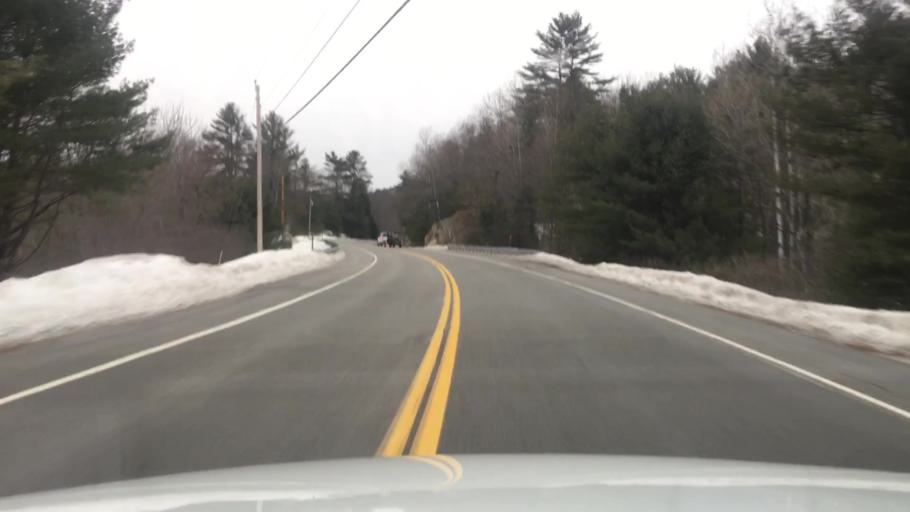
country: US
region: Maine
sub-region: York County
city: Limerick
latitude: 43.7274
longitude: -70.8140
